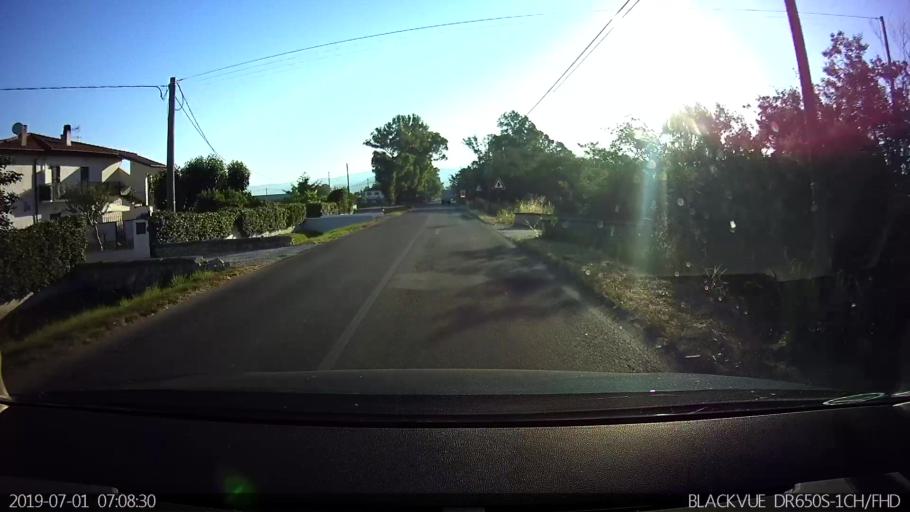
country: IT
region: Latium
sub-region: Provincia di Latina
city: Borgo Hermada
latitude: 41.2978
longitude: 13.1508
